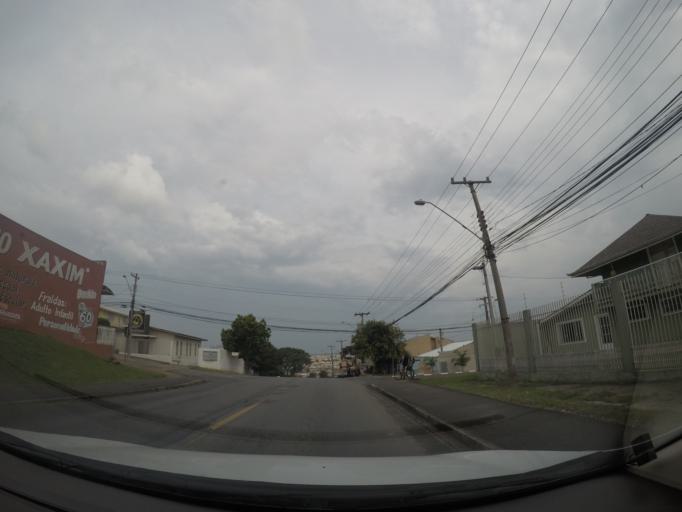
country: BR
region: Parana
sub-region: Sao Jose Dos Pinhais
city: Sao Jose dos Pinhais
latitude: -25.5256
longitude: -49.2609
